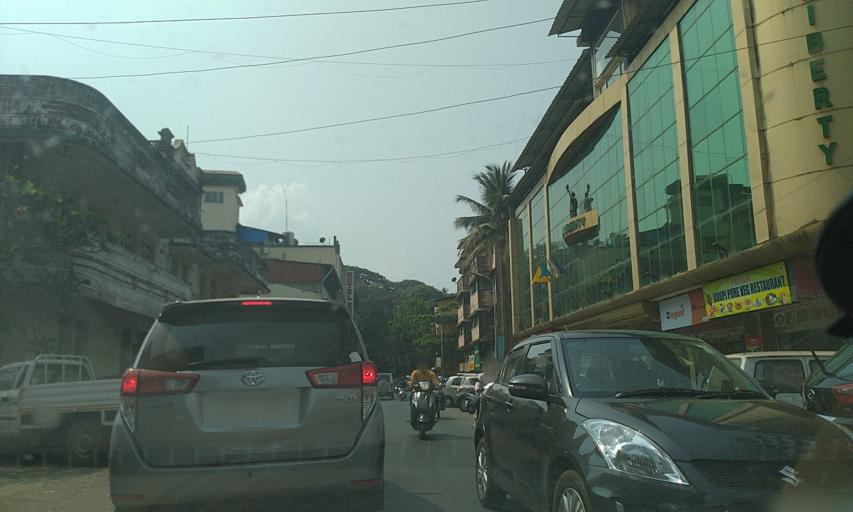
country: IN
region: Goa
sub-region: North Goa
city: Panaji
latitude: 15.4968
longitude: 73.8225
